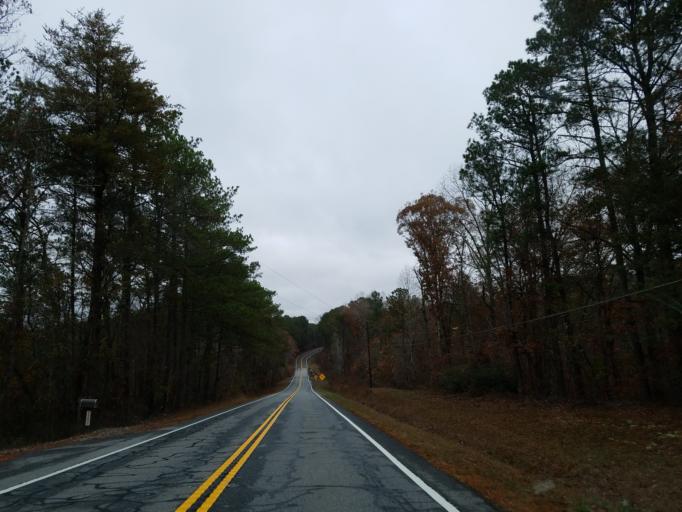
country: US
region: Georgia
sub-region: Cherokee County
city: Canton
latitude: 34.2618
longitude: -84.5975
